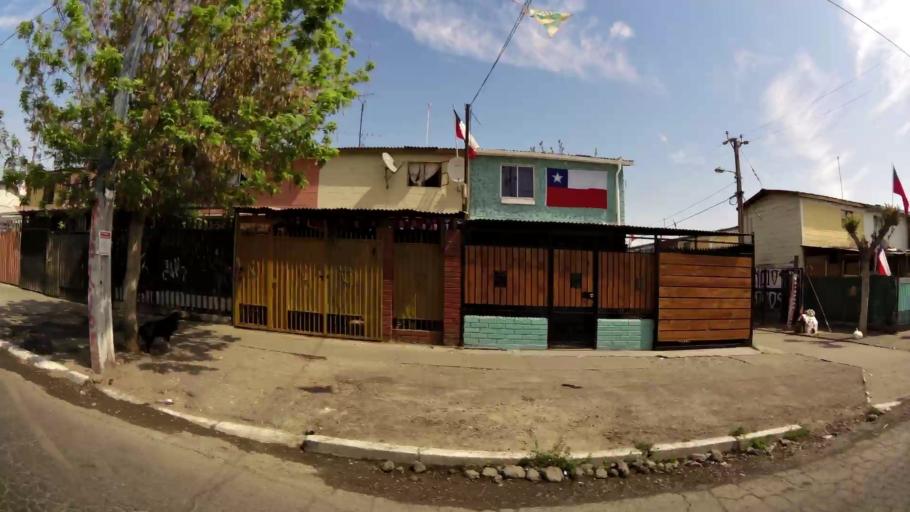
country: CL
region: Santiago Metropolitan
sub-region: Provincia de Cordillera
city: Puente Alto
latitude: -33.5903
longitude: -70.6008
